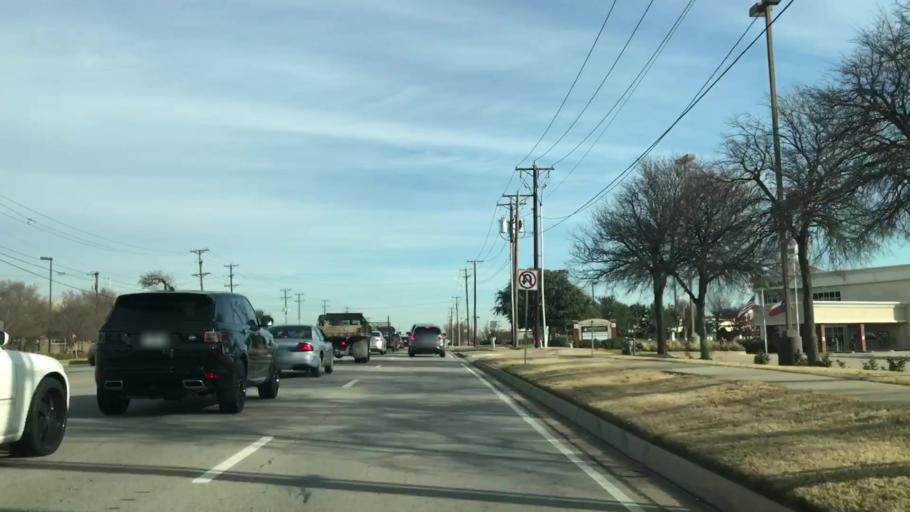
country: US
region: Texas
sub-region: Tarrant County
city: Colleyville
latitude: 32.9045
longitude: -97.1930
